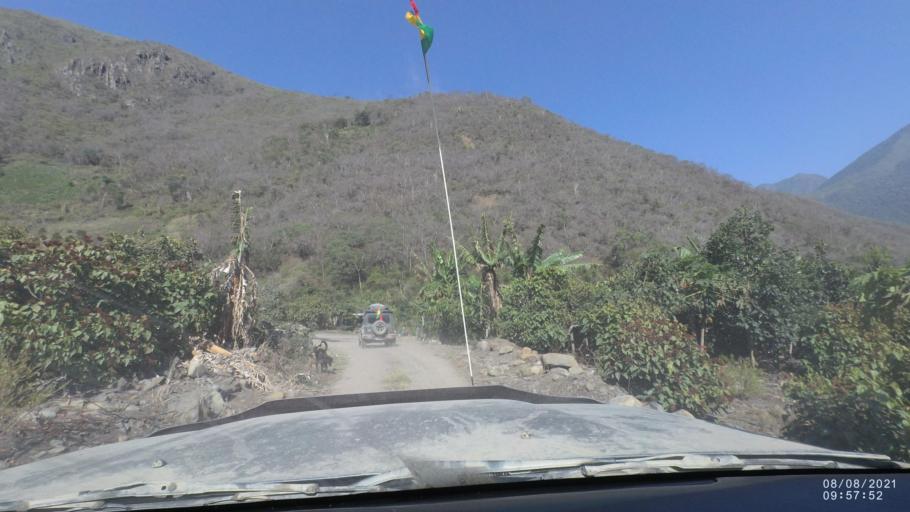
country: BO
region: La Paz
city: Quime
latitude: -16.6426
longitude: -66.7261
